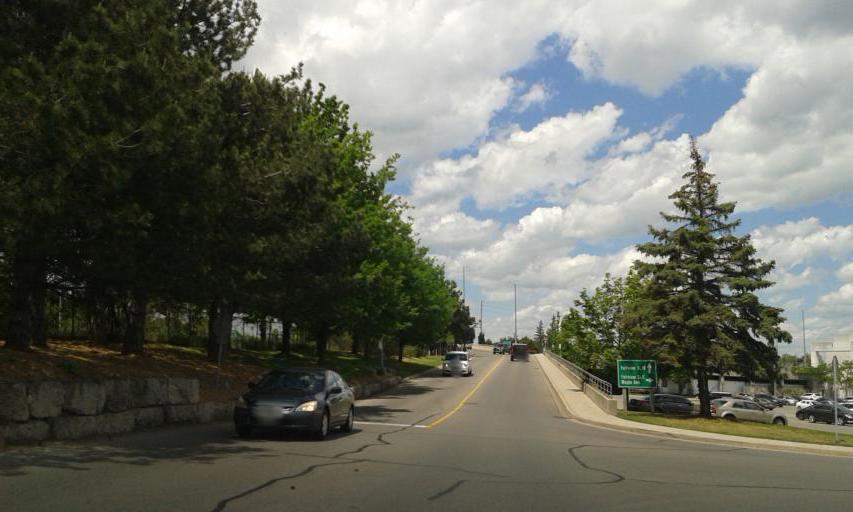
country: CA
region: Ontario
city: Burlington
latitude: 43.3261
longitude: -79.8225
